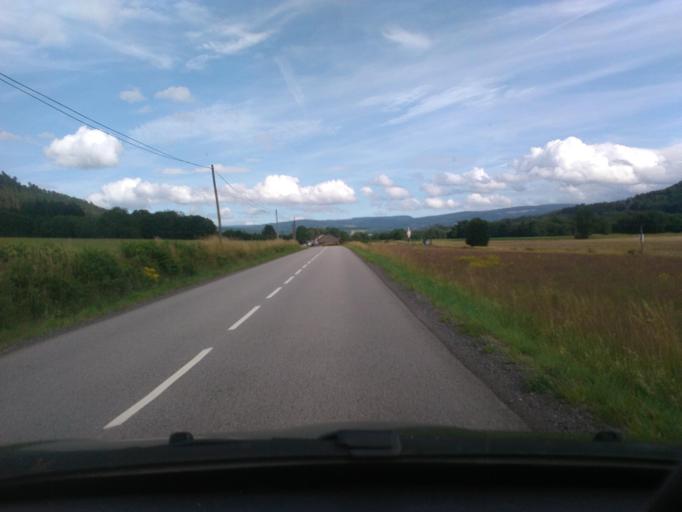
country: FR
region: Lorraine
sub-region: Departement des Vosges
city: Corcieux
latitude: 48.2052
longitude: 6.8392
